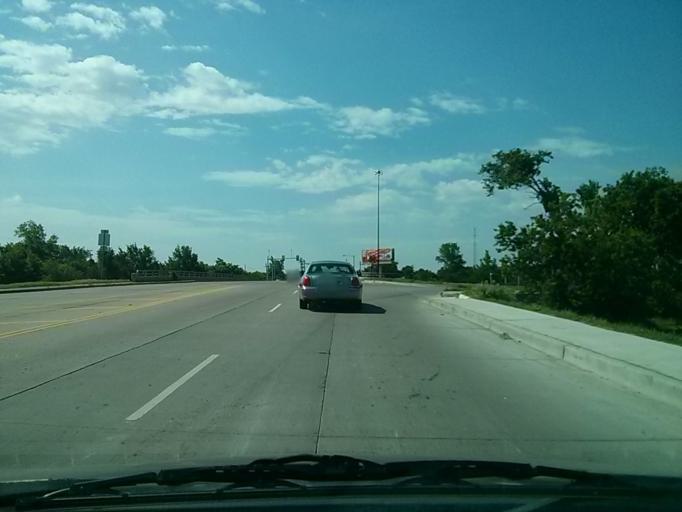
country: US
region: Oklahoma
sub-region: Tulsa County
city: Tulsa
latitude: 36.1763
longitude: -95.9757
